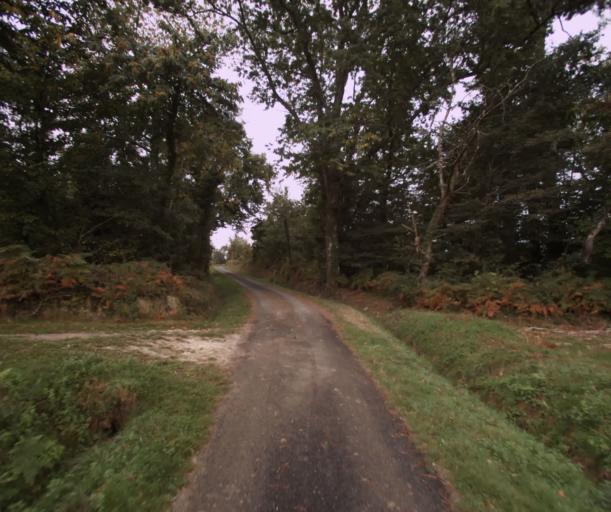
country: FR
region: Midi-Pyrenees
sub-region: Departement du Gers
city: Cazaubon
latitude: 43.8836
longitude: -0.0863
